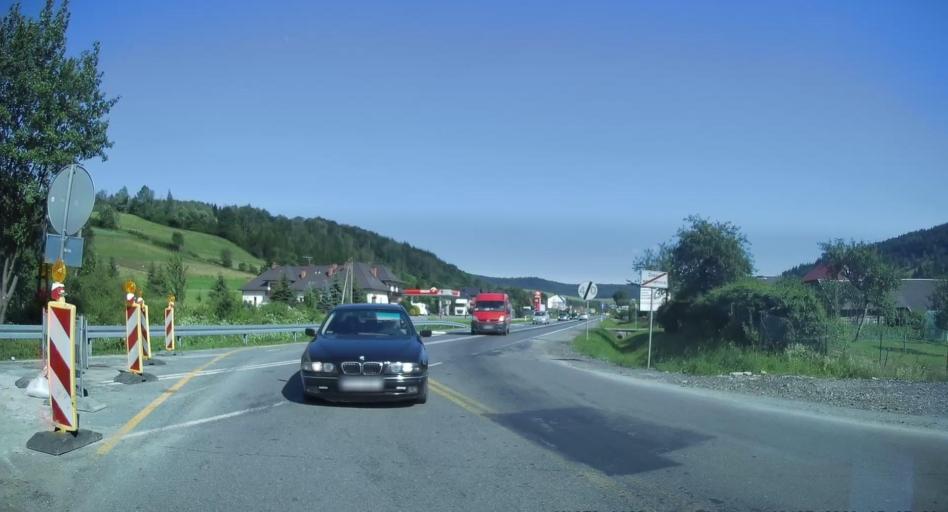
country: PL
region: Lesser Poland Voivodeship
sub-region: Powiat nowosadecki
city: Labowa
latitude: 49.5061
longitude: 20.8928
